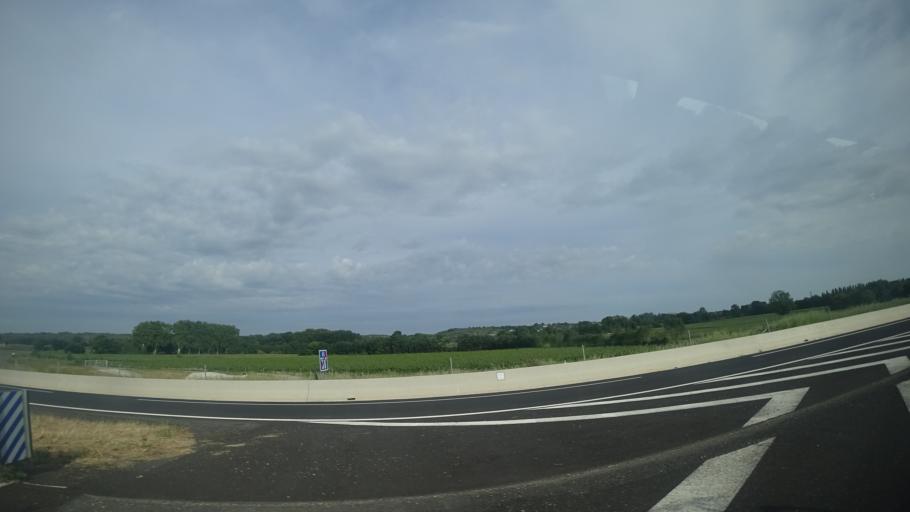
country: FR
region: Languedoc-Roussillon
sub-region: Departement de l'Herault
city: Pezenas
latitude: 43.4513
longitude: 3.4290
